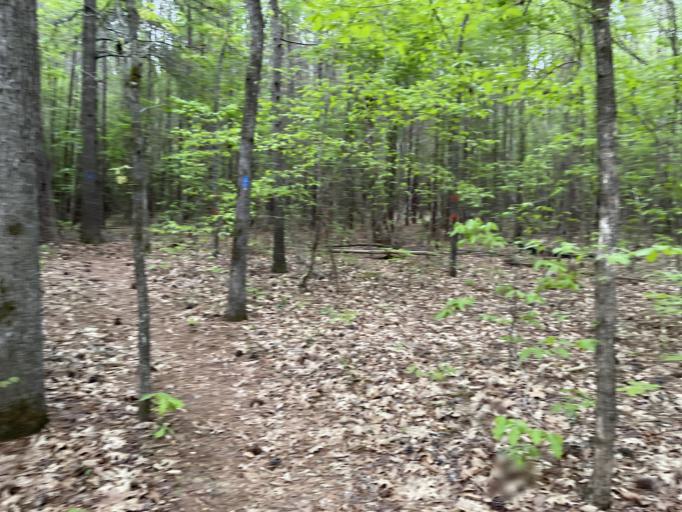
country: US
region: North Carolina
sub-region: Durham County
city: Gorman
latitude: 36.0734
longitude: -78.8359
